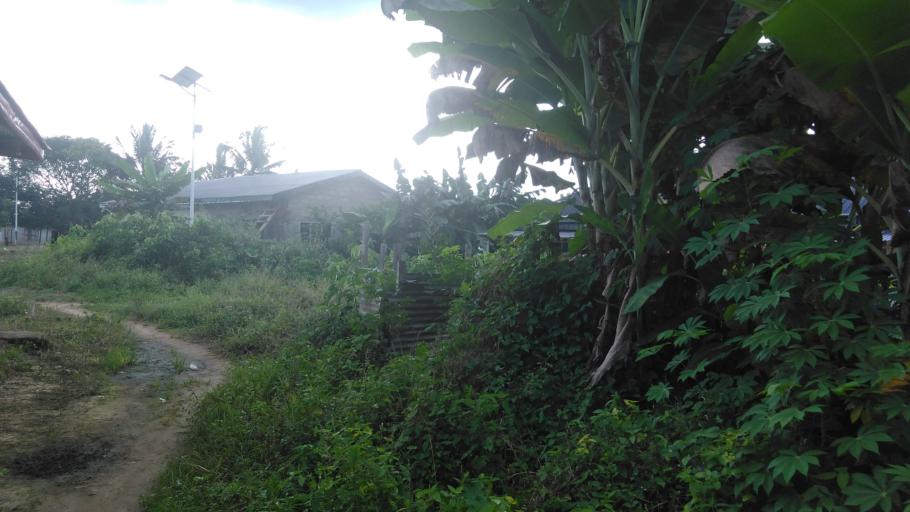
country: NG
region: Edo
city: Siluko
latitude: 6.1451
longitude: 5.2009
